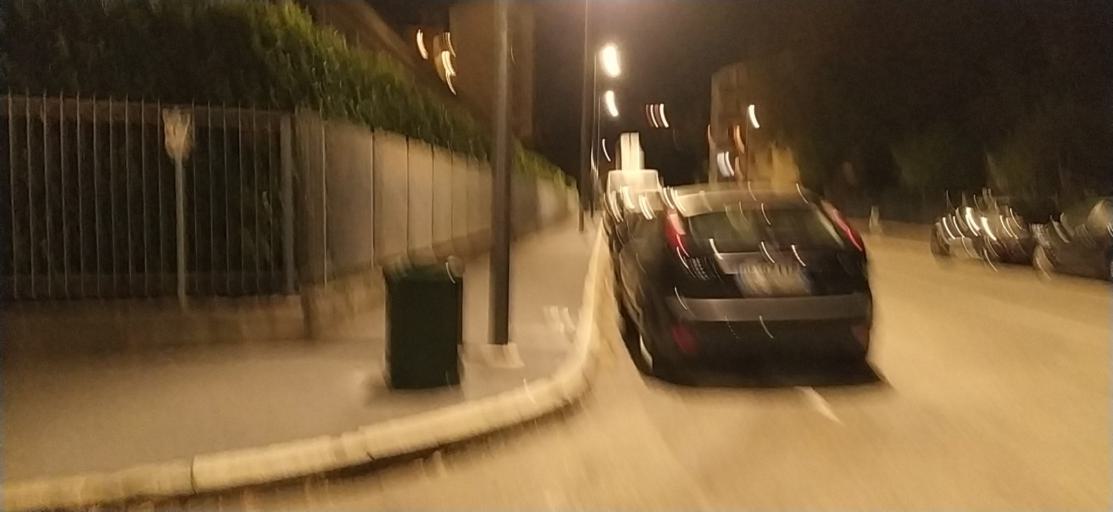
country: IT
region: Lombardy
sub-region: Citta metropolitana di Milano
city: Novate Milanese
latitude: 45.5128
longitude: 9.1461
